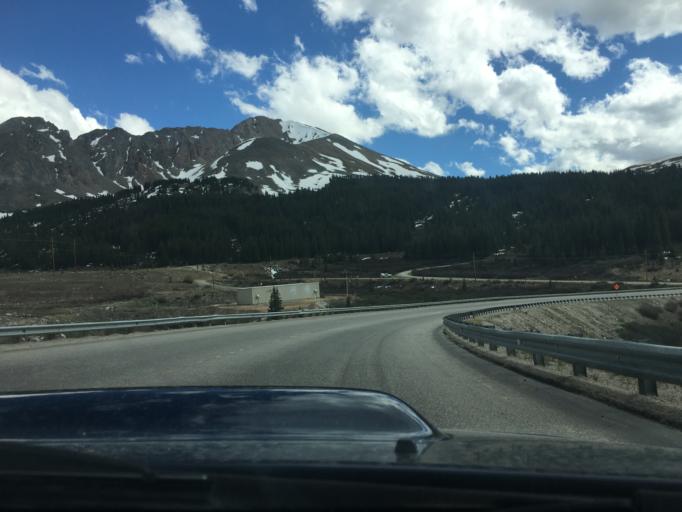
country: US
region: Colorado
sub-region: Lake County
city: Leadville
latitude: 39.3617
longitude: -106.1786
